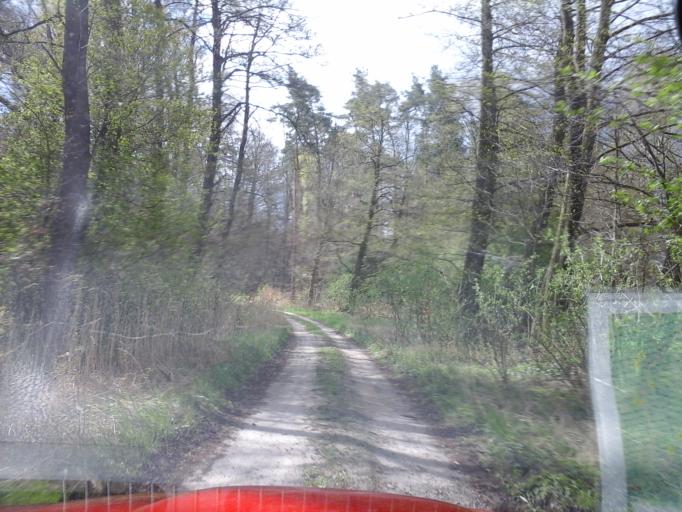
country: PL
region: West Pomeranian Voivodeship
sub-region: Powiat choszczenski
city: Bierzwnik
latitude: 53.0373
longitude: 15.5981
